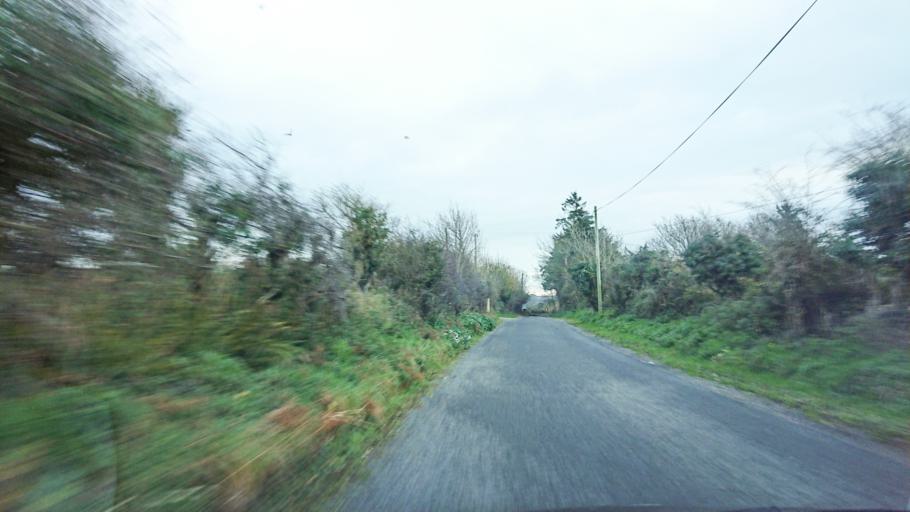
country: IE
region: Munster
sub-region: Waterford
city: Dunmore East
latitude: 52.2389
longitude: -6.9782
